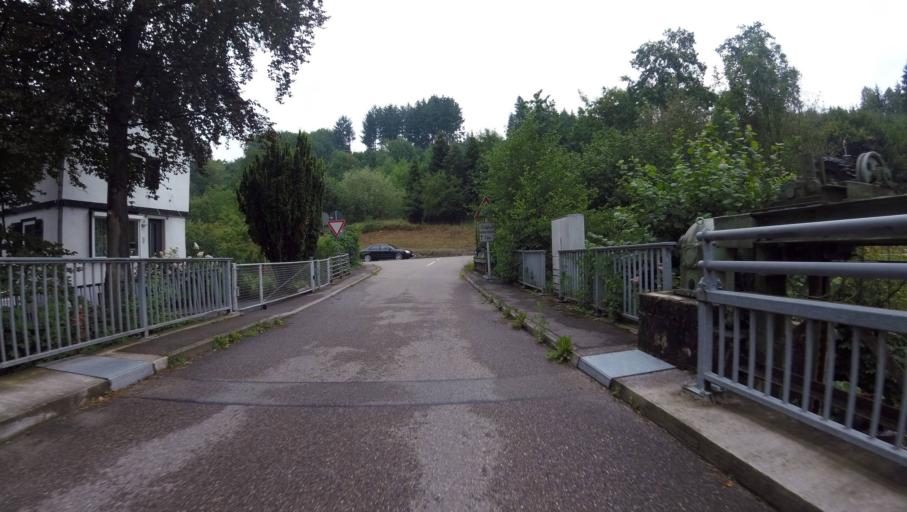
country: DE
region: Baden-Wuerttemberg
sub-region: Regierungsbezirk Stuttgart
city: Oppenweiler
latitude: 48.9924
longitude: 9.4687
